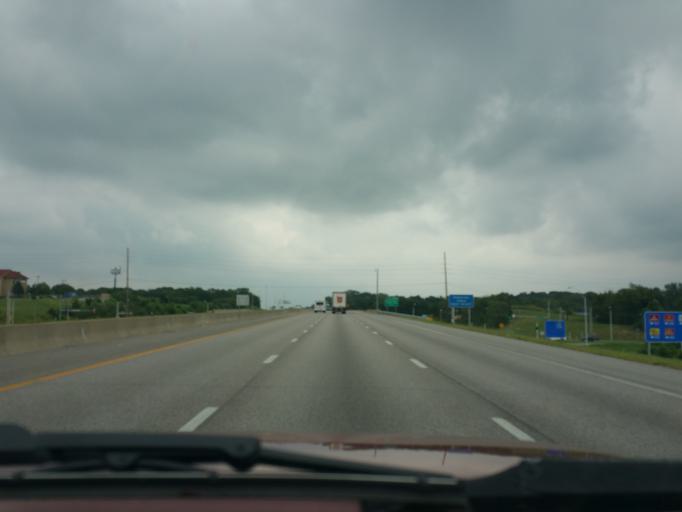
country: US
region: Kansas
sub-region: Wyandotte County
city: Edwardsville
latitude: 39.1050
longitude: -94.7627
